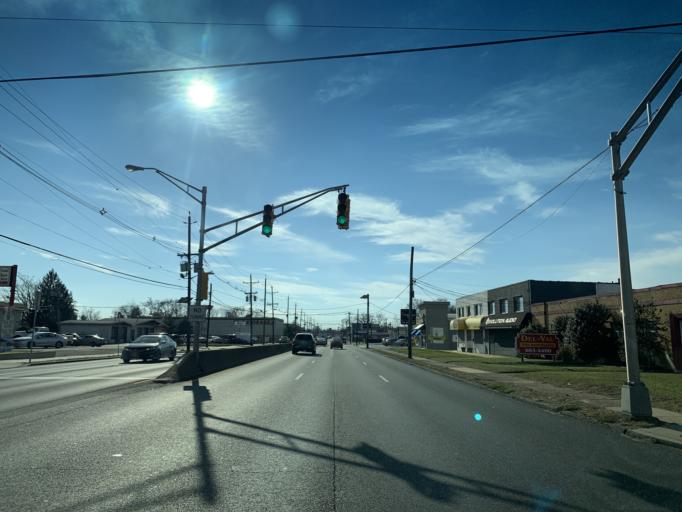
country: US
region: New Jersey
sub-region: Camden County
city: Merchantville
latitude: 39.9415
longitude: -75.0725
